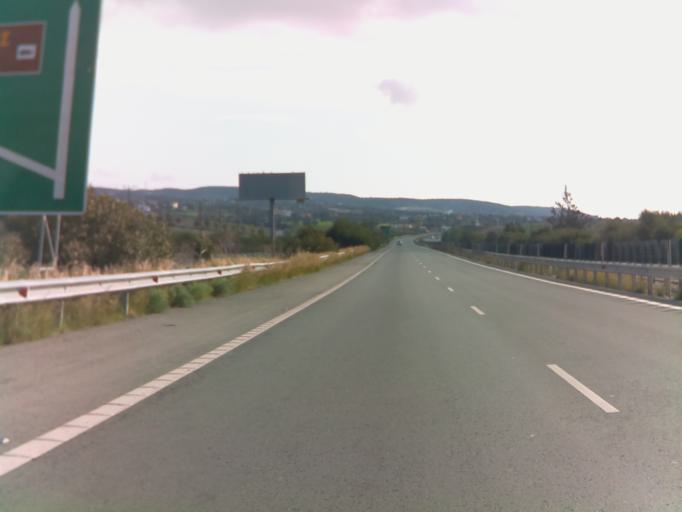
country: CY
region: Limassol
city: Pyrgos
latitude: 34.7336
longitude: 33.2212
